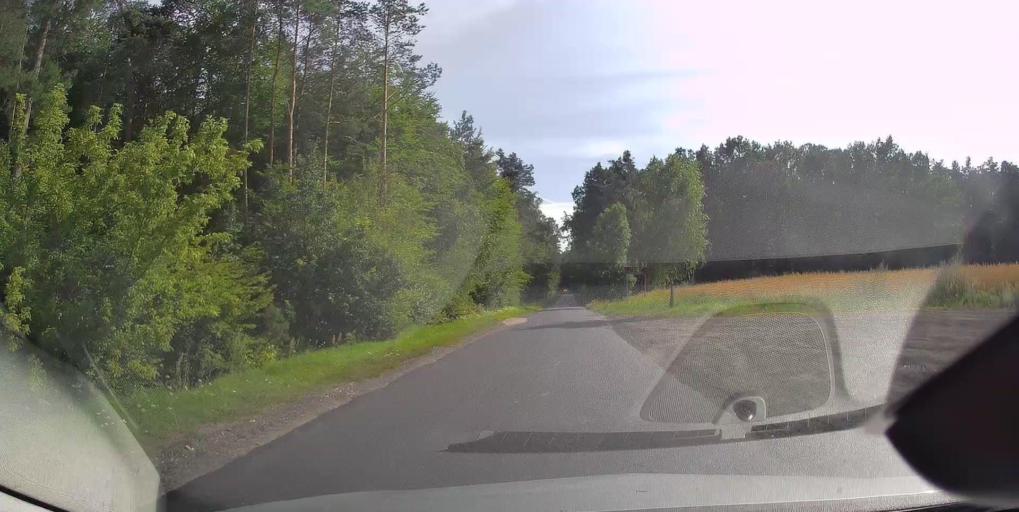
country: PL
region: Lodz Voivodeship
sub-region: Powiat opoczynski
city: Mniszkow
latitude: 51.4416
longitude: 20.0258
